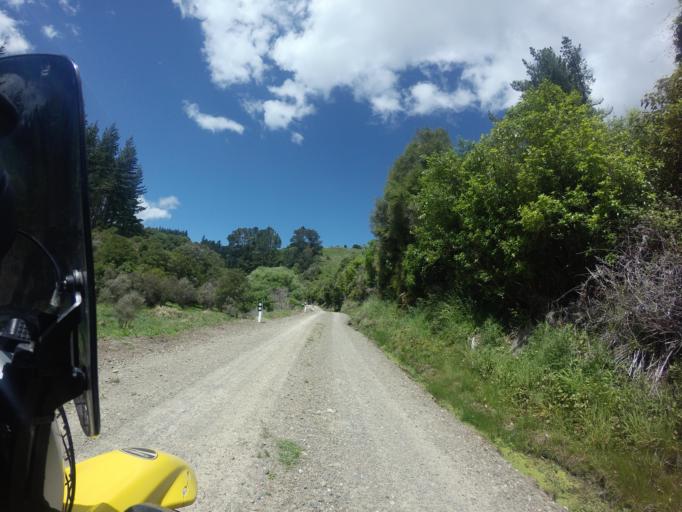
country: NZ
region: Hawke's Bay
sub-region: Wairoa District
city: Wairoa
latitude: -38.9736
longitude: 177.6776
